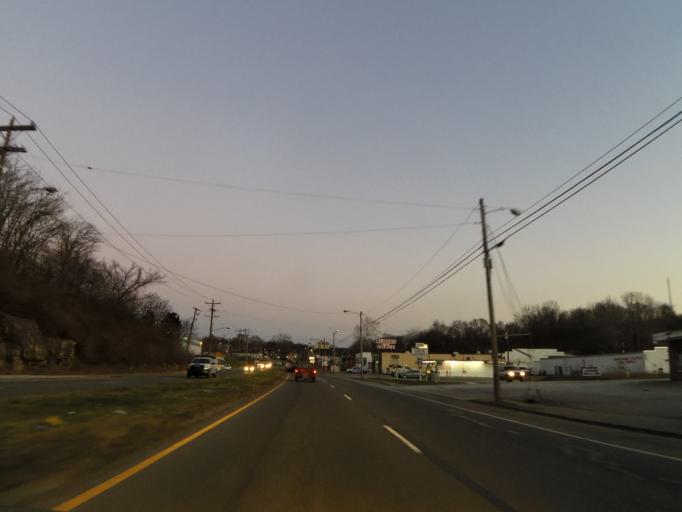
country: US
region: Tennessee
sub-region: Davidson County
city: Nashville
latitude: 36.1326
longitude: -86.7579
